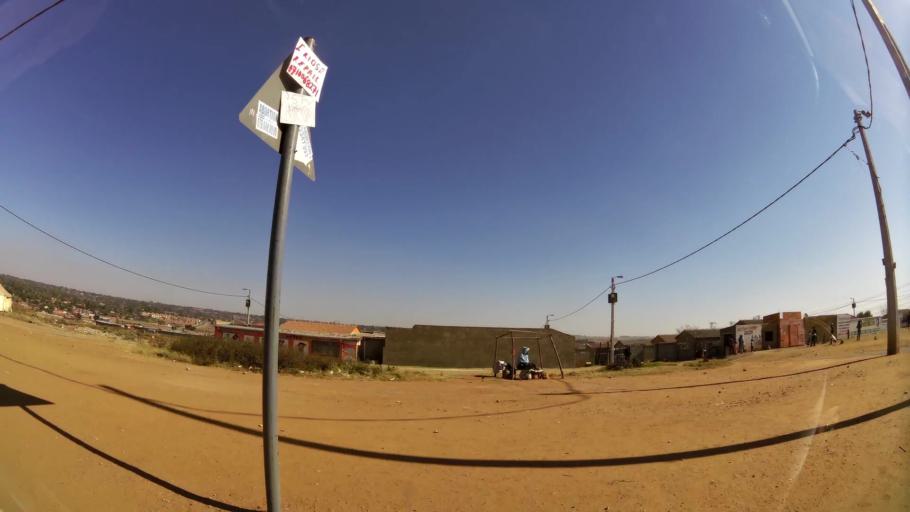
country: ZA
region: Gauteng
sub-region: Ekurhuleni Metropolitan Municipality
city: Tembisa
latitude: -26.0319
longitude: 28.2243
